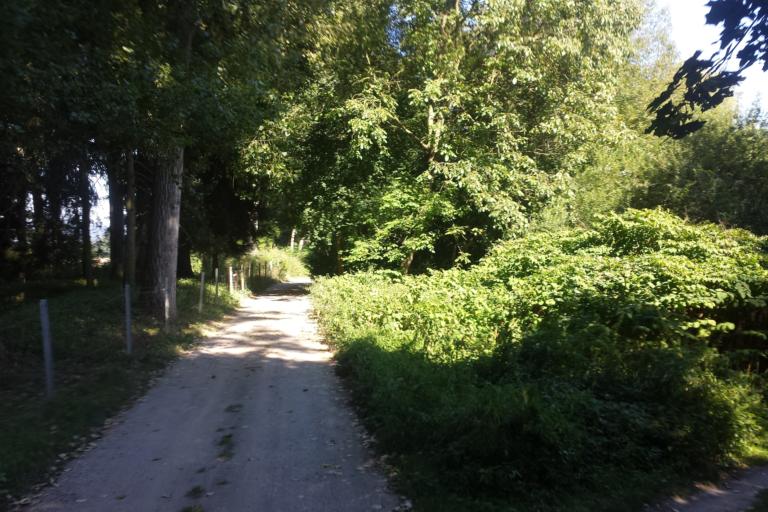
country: DE
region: Hesse
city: Viernheim
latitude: 49.5924
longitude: 8.5928
